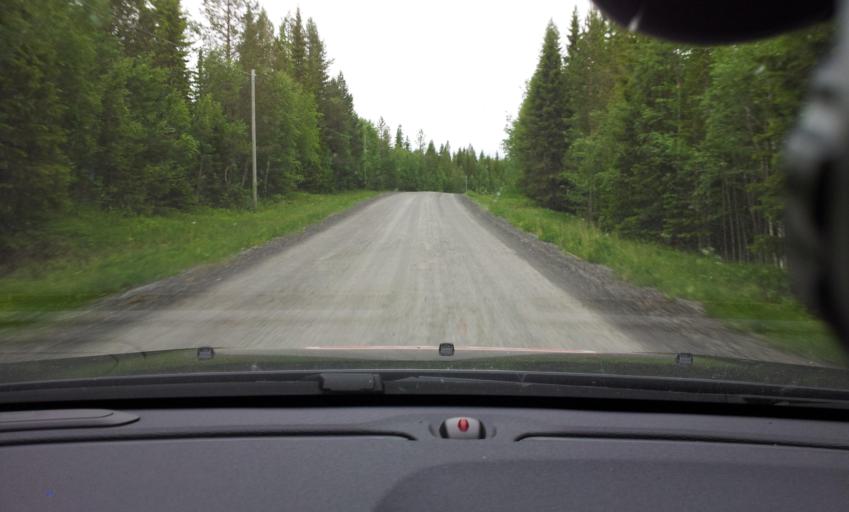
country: SE
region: Jaemtland
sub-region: Are Kommun
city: Jarpen
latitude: 63.2852
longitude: 13.6423
